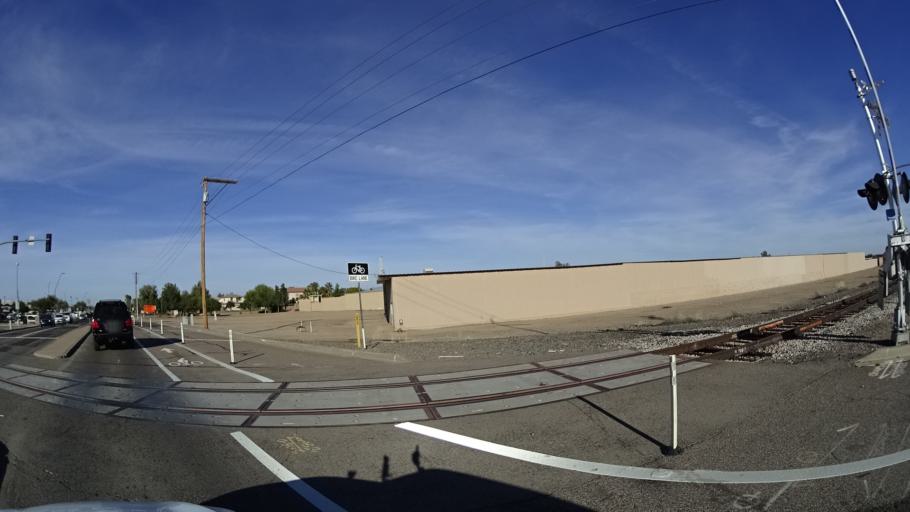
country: US
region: Arizona
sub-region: Maricopa County
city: Queen Creek
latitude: 33.2563
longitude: -111.6346
